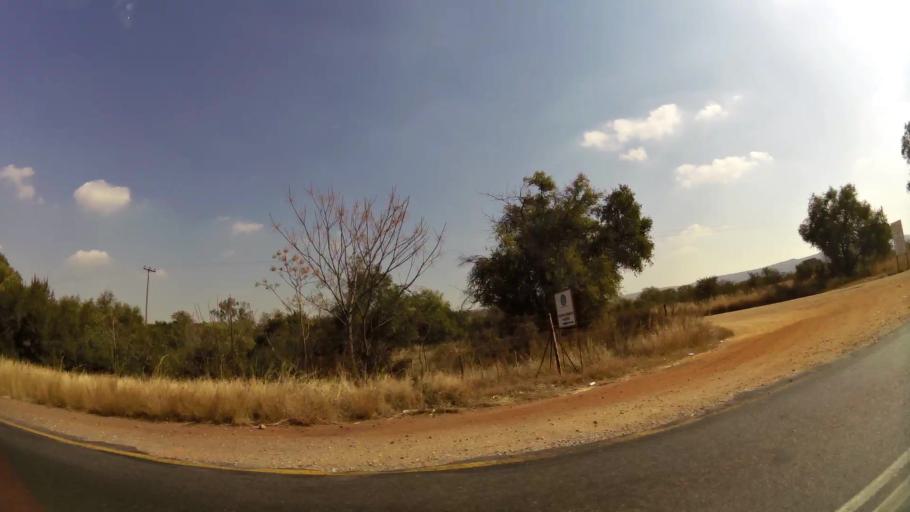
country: ZA
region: North-West
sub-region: Bojanala Platinum District Municipality
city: Rustenburg
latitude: -25.5167
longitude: 27.1013
